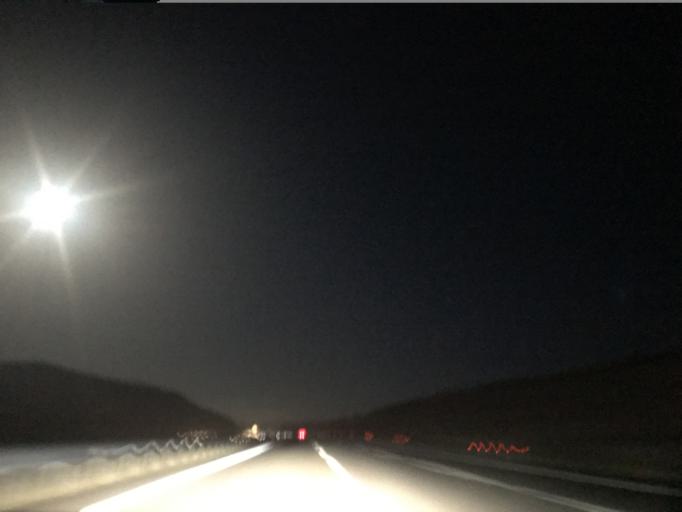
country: TR
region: Nigde
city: Ulukisla
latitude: 37.6425
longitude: 34.3776
